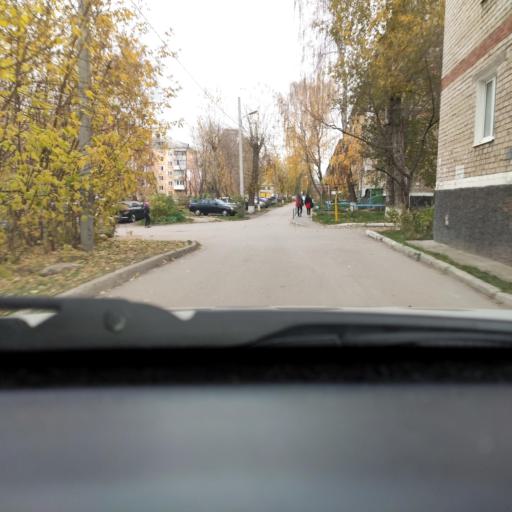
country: RU
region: Perm
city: Kondratovo
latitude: 57.9708
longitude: 56.1572
